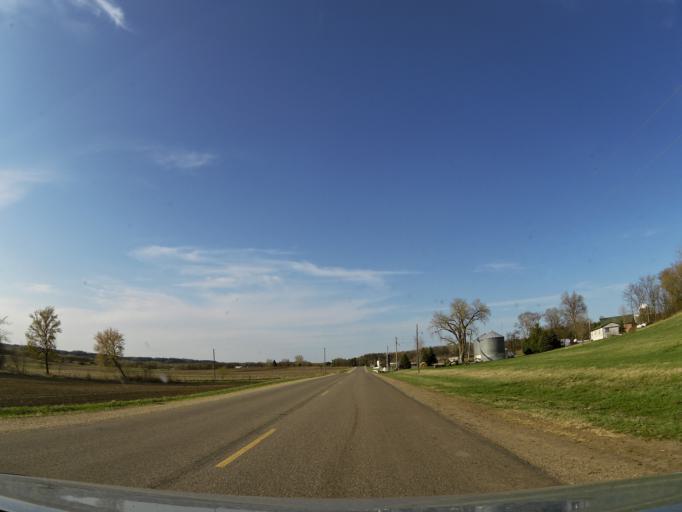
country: US
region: Wisconsin
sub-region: Pierce County
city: River Falls
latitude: 44.7947
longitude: -92.6462
